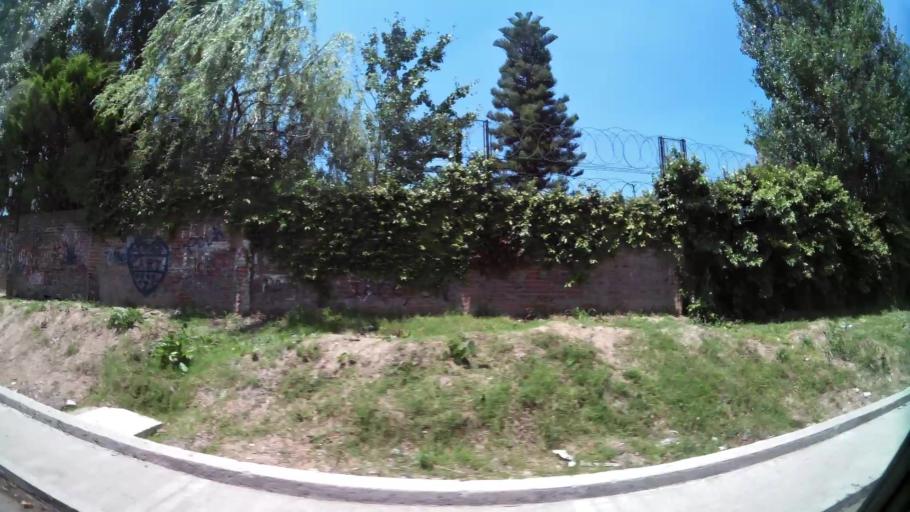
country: AR
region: Buenos Aires
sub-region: Partido de Tigre
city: Tigre
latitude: -34.4308
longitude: -58.5963
